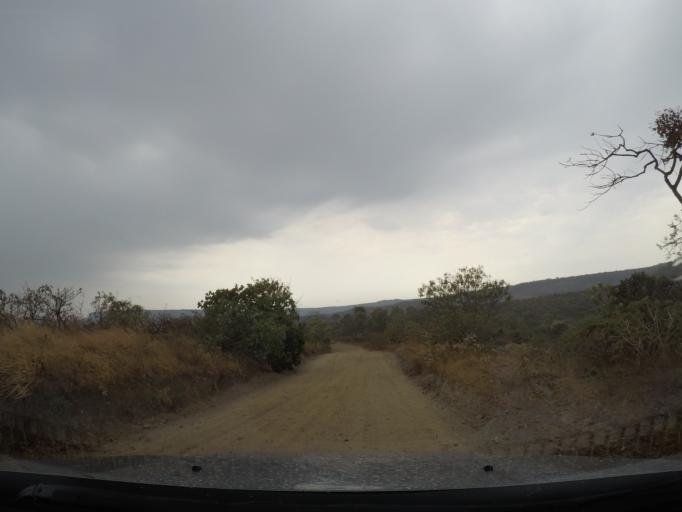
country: BR
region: Goias
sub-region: Pirenopolis
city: Pirenopolis
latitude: -15.8238
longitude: -48.9069
